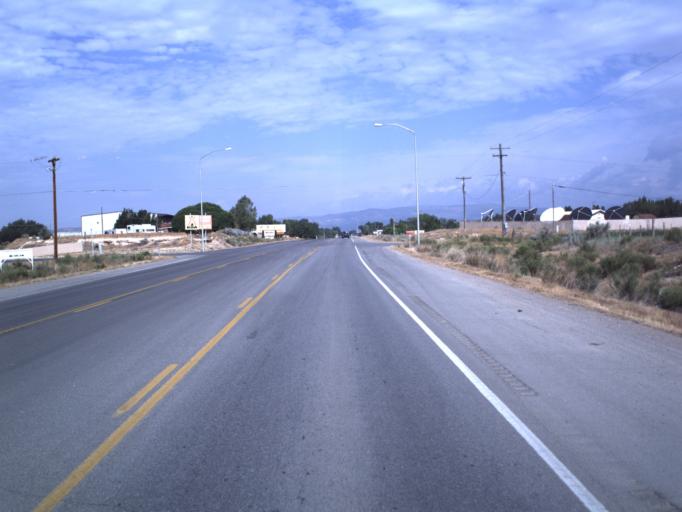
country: US
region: Utah
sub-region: Uintah County
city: Naples
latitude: 40.4056
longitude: -109.4788
